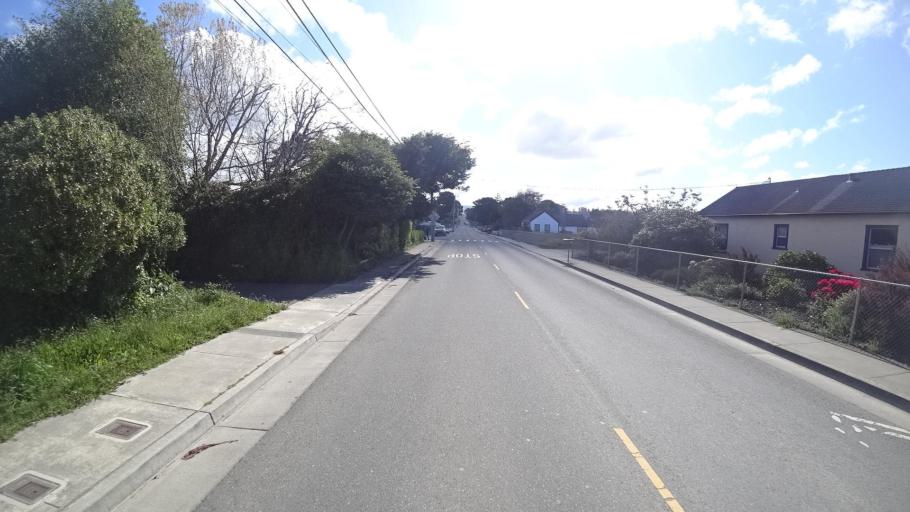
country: US
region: California
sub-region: Humboldt County
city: McKinleyville
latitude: 40.9344
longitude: -124.1193
